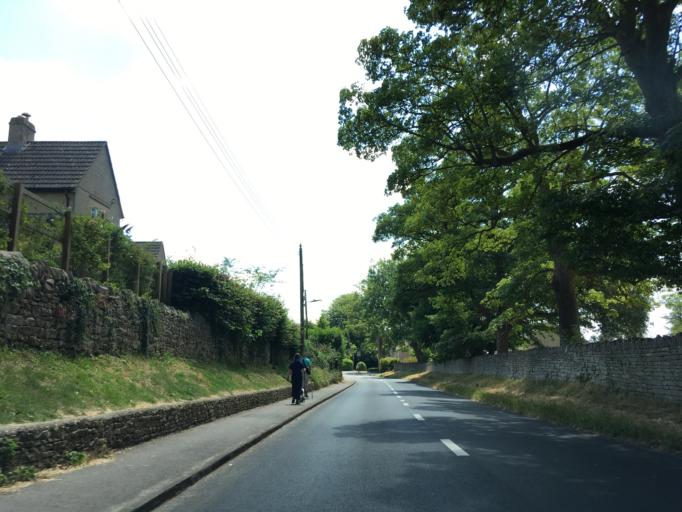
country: GB
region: England
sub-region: Gloucestershire
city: Painswick
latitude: 51.7913
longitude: -2.1951
